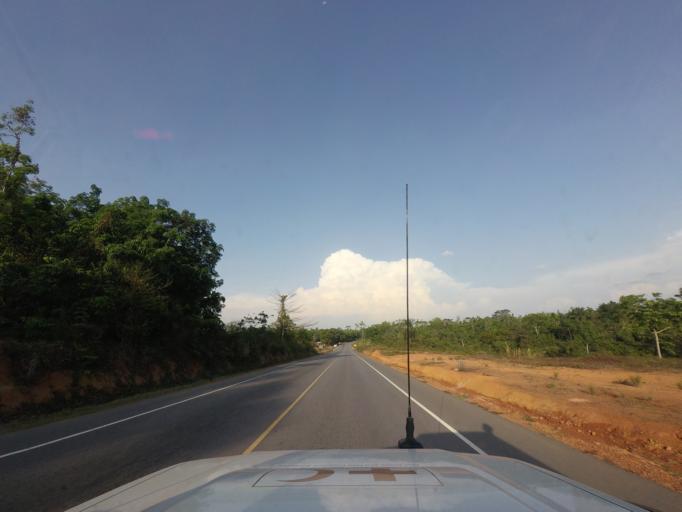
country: LR
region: Bong
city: Gbarnga
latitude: 7.0081
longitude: -9.3605
